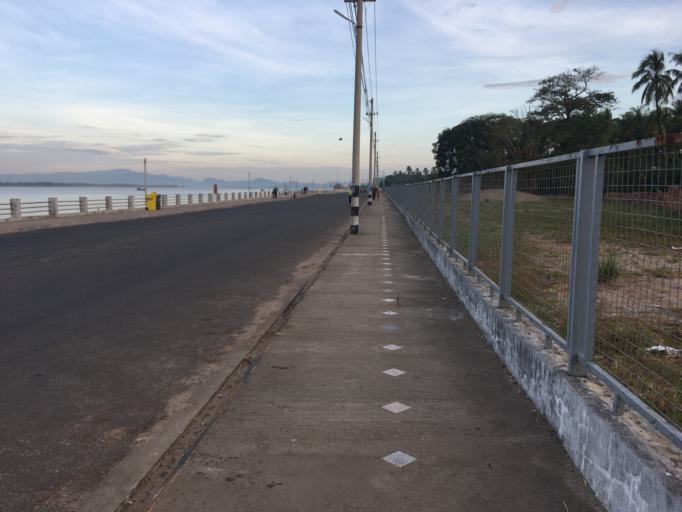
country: MM
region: Mon
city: Mawlamyine
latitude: 16.4591
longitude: 97.6234
